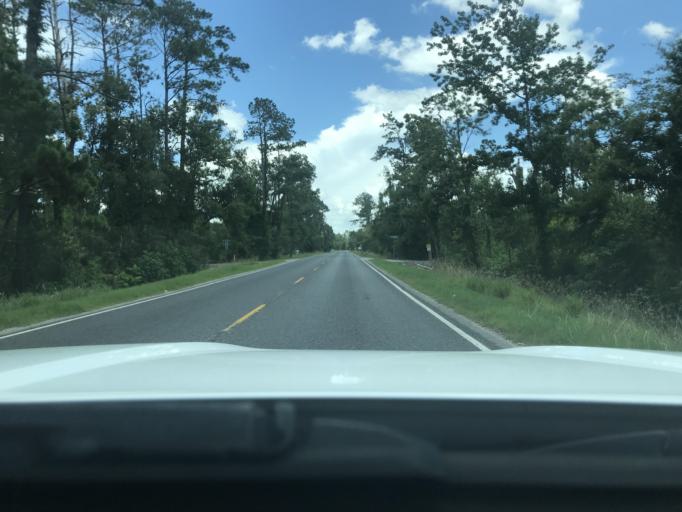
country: US
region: Louisiana
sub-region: Calcasieu Parish
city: Moss Bluff
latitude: 30.2771
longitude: -93.1752
